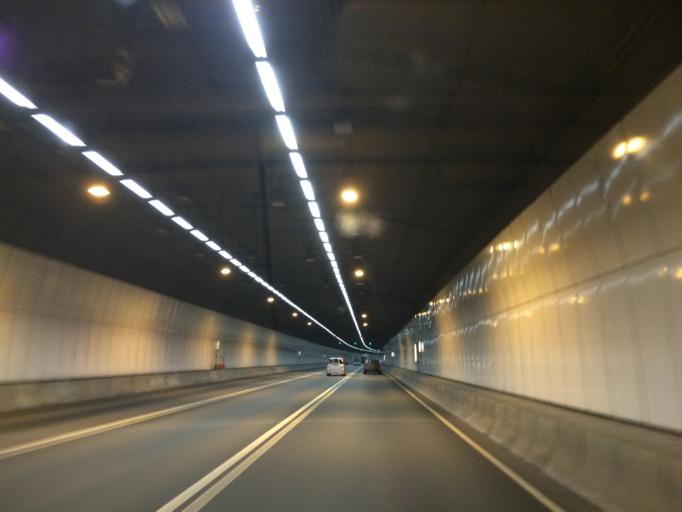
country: HK
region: Wong Tai Sin
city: Wong Tai Sin
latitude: 22.3571
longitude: 114.1624
